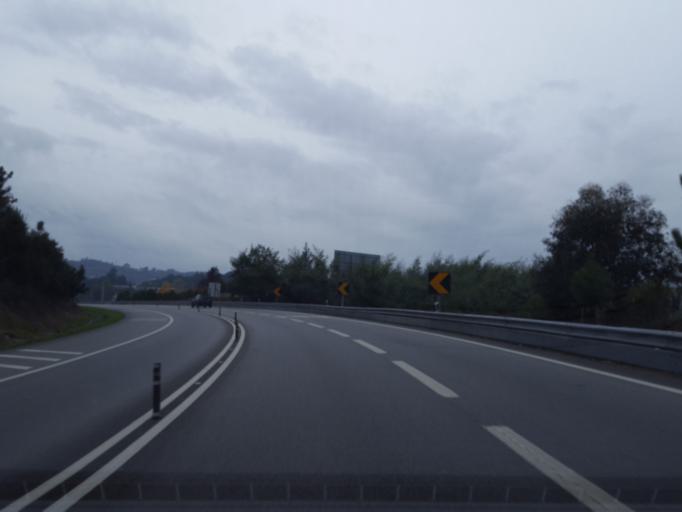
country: PT
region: Porto
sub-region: Marco de Canaveses
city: Marco de Canavezes
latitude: 41.2171
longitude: -8.1745
